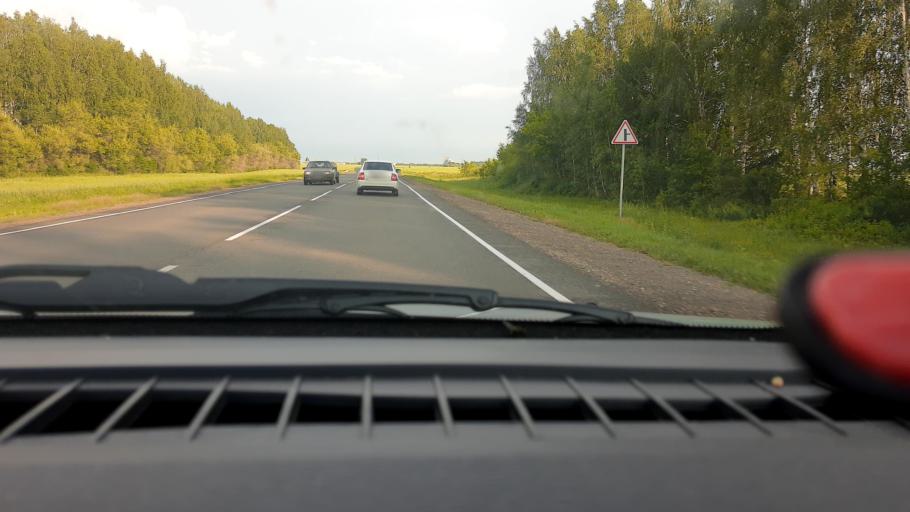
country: RU
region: Nizjnij Novgorod
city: Shatki
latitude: 55.2268
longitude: 44.0672
